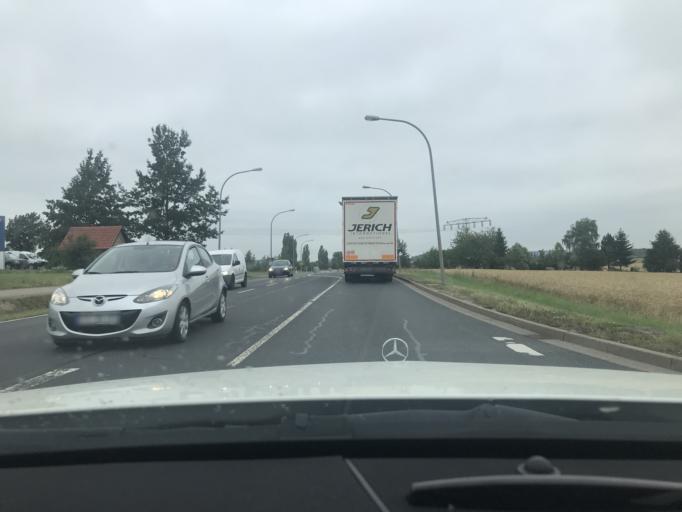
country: DE
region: Thuringia
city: Leinefelde
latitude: 51.3947
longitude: 10.3275
